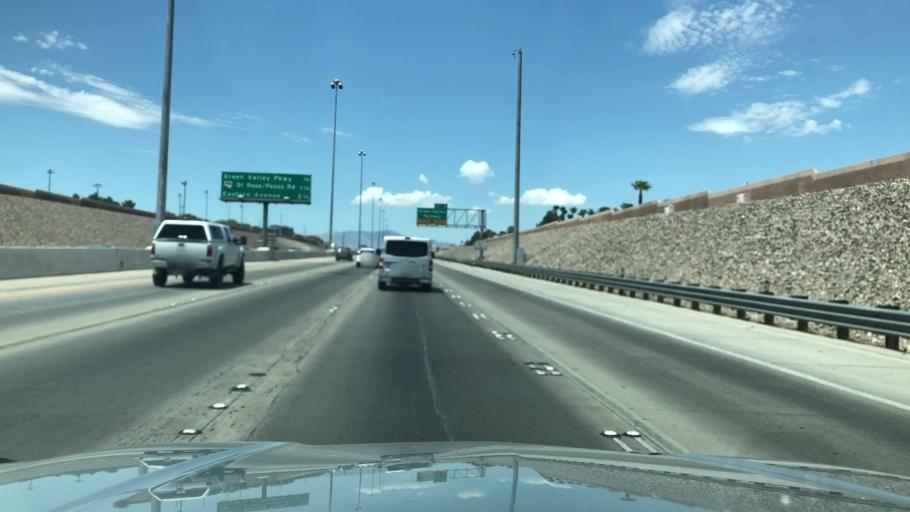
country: US
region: Nevada
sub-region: Clark County
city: Whitney
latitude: 36.0262
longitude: -115.0731
